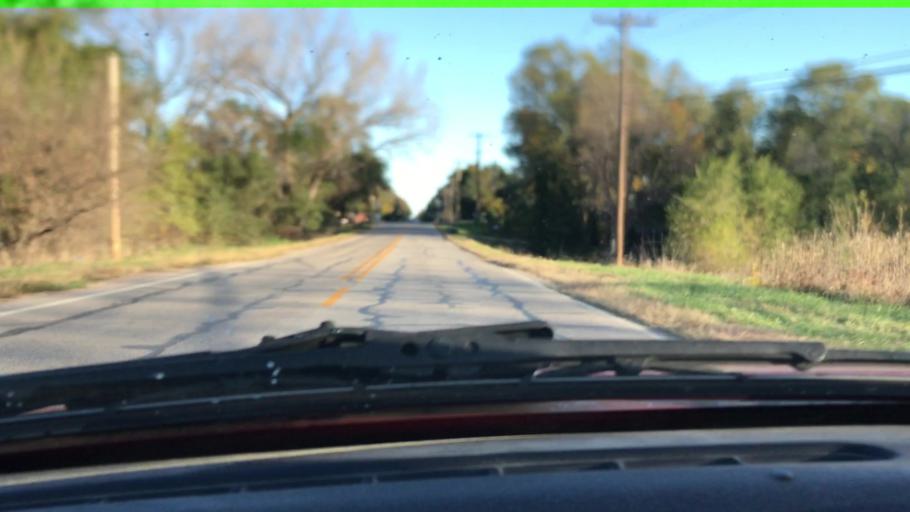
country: US
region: Nebraska
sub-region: Lancaster County
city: Lincoln
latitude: 40.7754
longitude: -96.7495
